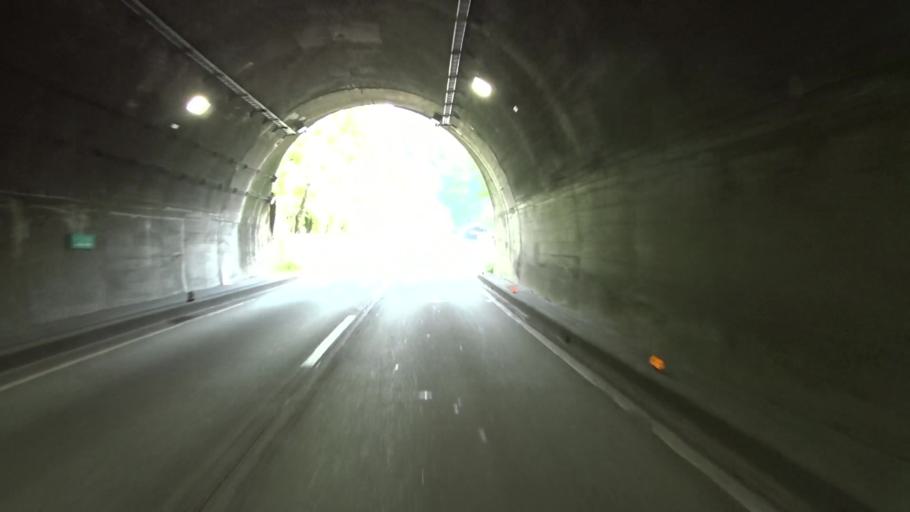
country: JP
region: Shiga Prefecture
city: Otsu-shi
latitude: 35.0206
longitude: 135.8482
